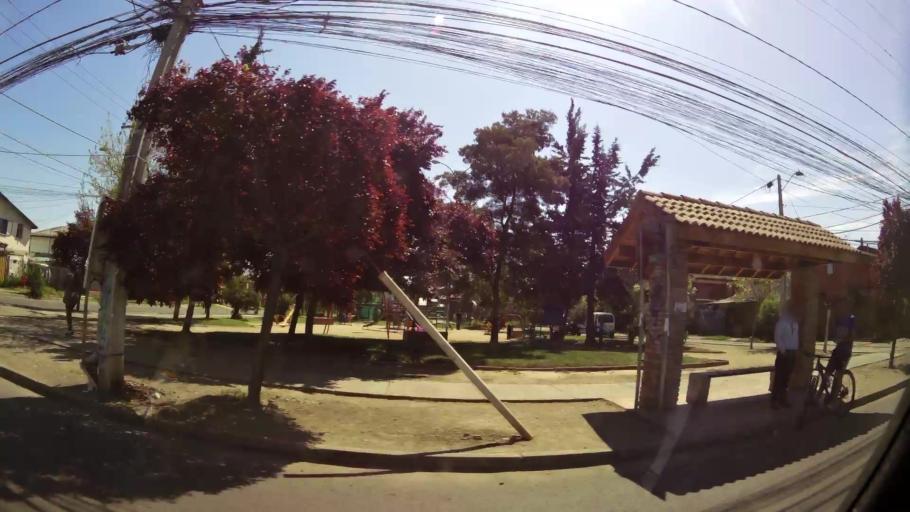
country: CL
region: Santiago Metropolitan
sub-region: Provincia de Talagante
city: Talagante
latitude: -33.6530
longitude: -70.9049
